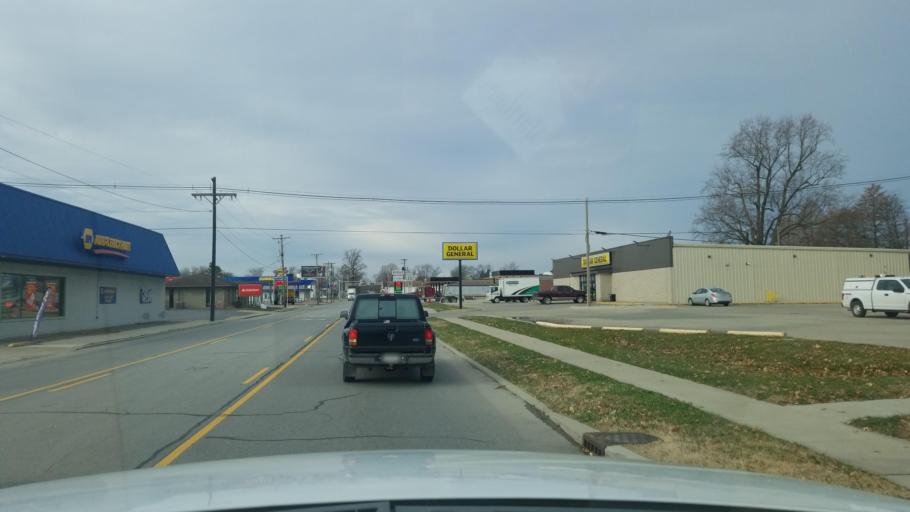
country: US
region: Indiana
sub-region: Posey County
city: Mount Vernon
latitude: 37.9309
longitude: -87.9007
